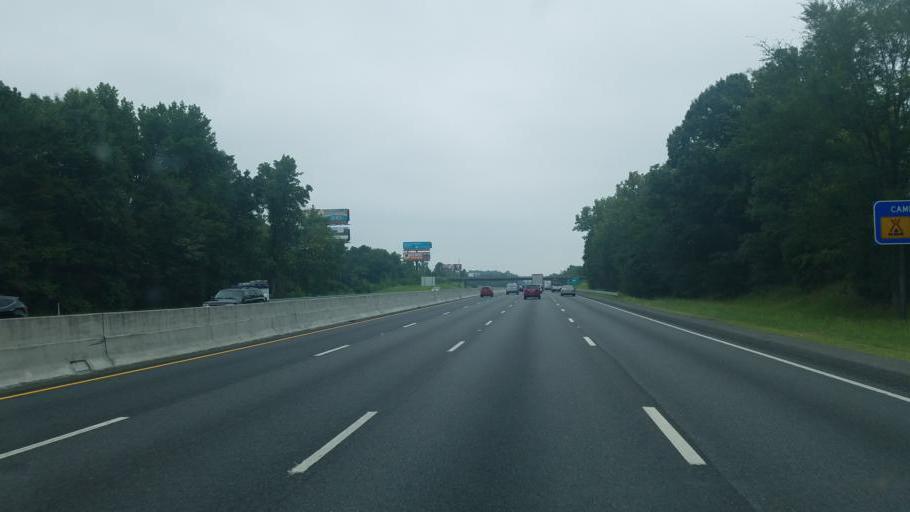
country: US
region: South Carolina
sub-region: York County
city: Fort Mill
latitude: 35.0397
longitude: -80.9600
